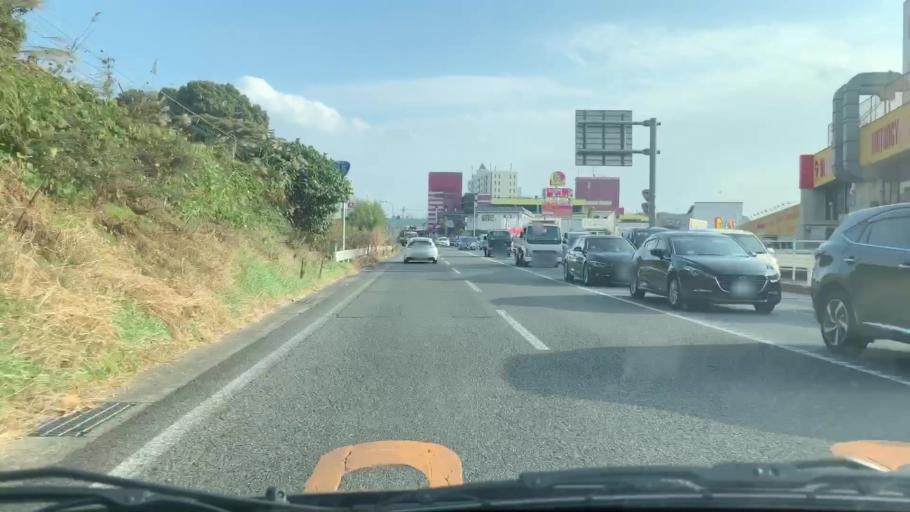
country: JP
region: Nagasaki
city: Sasebo
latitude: 33.1441
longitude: 129.7862
